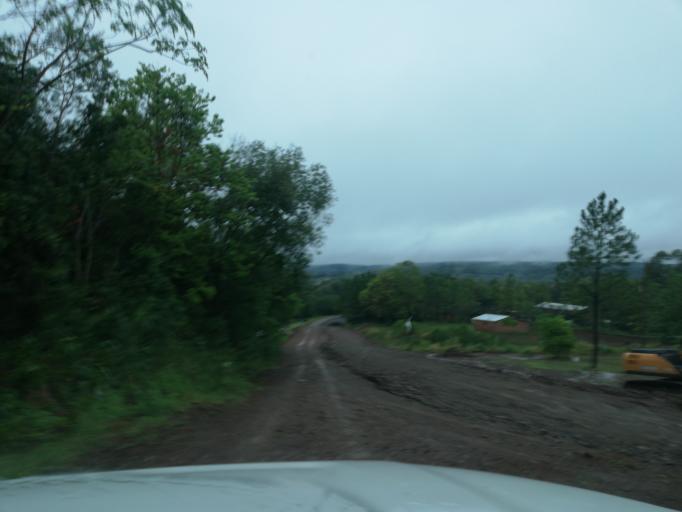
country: AR
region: Misiones
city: Almafuerte
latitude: -27.5374
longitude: -55.4091
